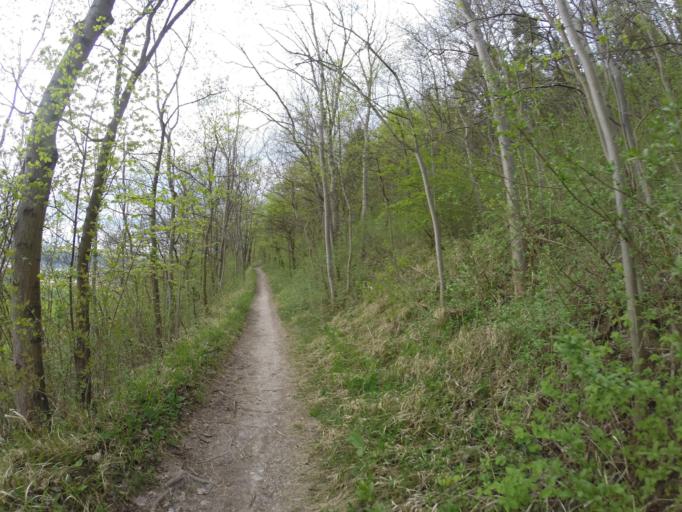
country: DE
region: Thuringia
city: Golmsdorf
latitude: 50.9588
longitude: 11.6454
